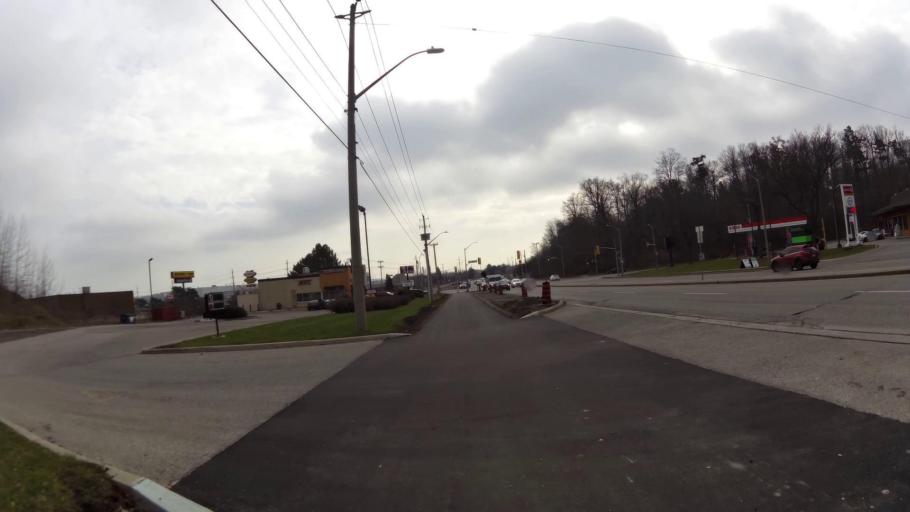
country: CA
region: Ontario
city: Kitchener
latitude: 43.4109
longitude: -80.4618
